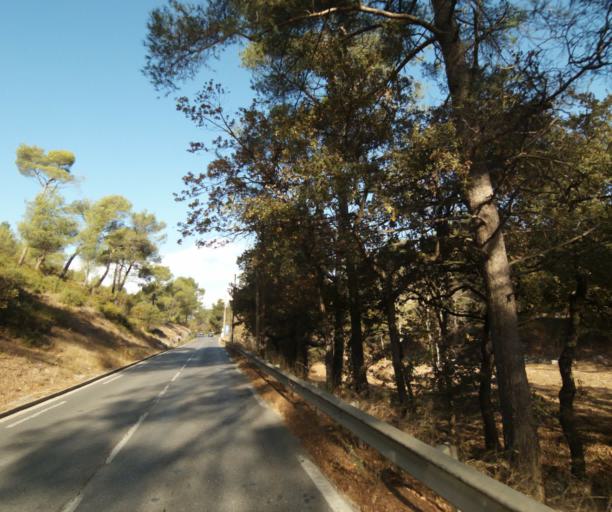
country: FR
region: Provence-Alpes-Cote d'Azur
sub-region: Departement des Bouches-du-Rhone
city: Allauch
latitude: 43.3143
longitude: 5.4984
